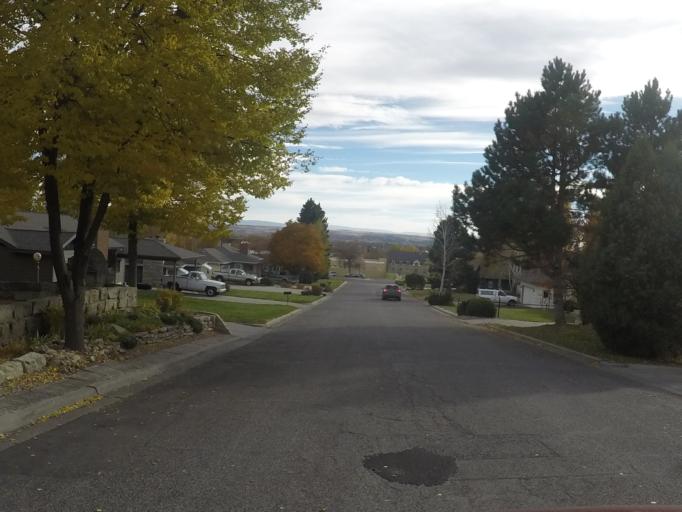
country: US
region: Montana
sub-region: Yellowstone County
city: Billings
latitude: 45.7999
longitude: -108.5564
